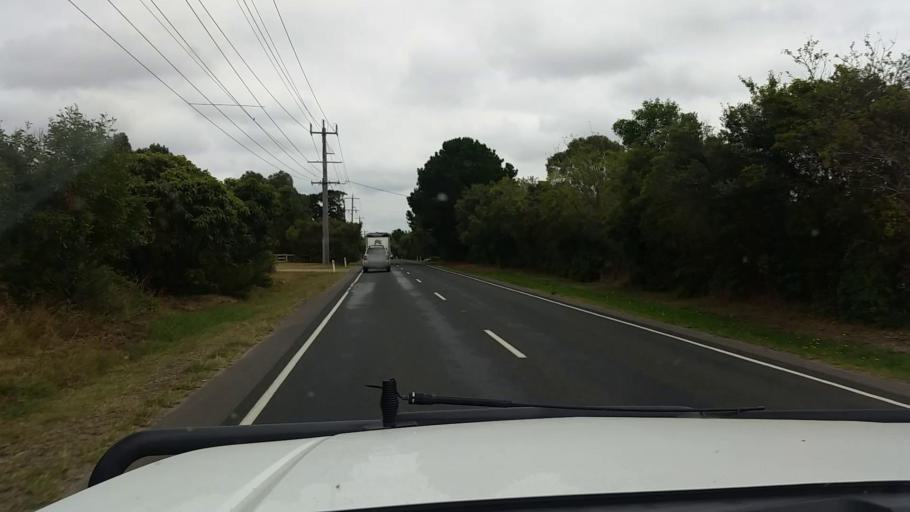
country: AU
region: Victoria
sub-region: Mornington Peninsula
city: Hastings
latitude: -38.2846
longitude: 145.1753
